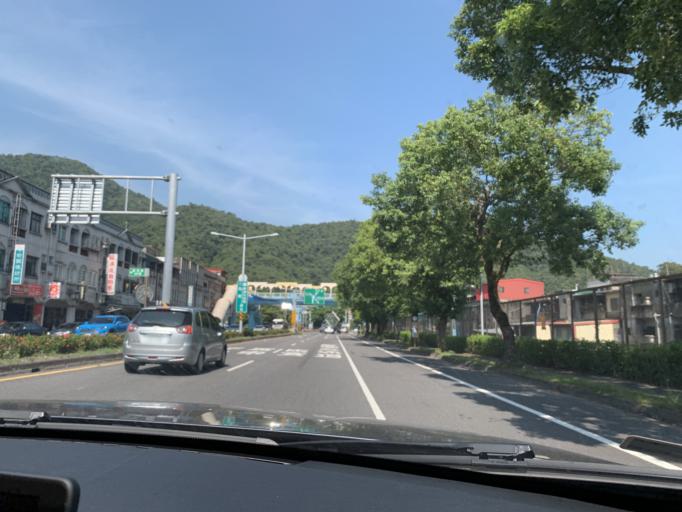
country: TW
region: Taiwan
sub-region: Yilan
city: Yilan
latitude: 24.5959
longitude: 121.8382
